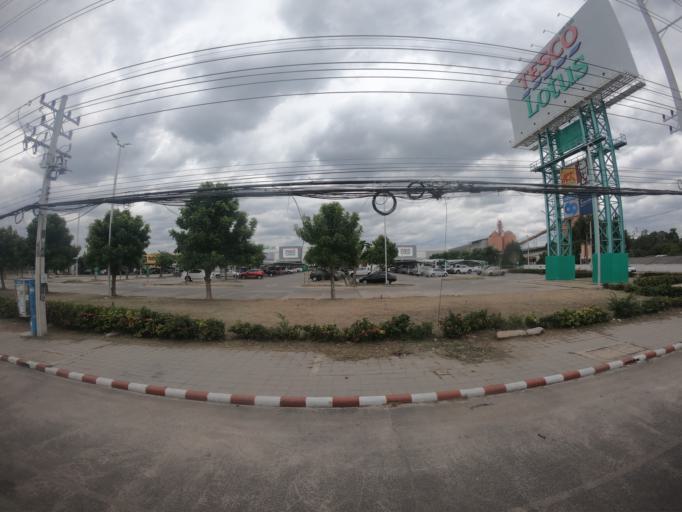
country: TH
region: Nakhon Ratchasima
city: Nakhon Ratchasima
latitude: 14.9484
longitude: 102.1259
